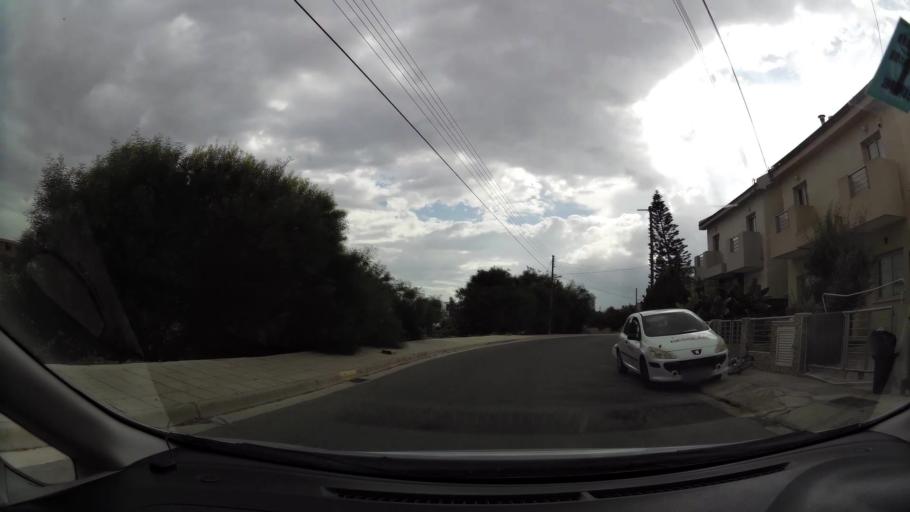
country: CY
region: Lefkosia
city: Geri
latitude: 35.1108
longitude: 33.3913
